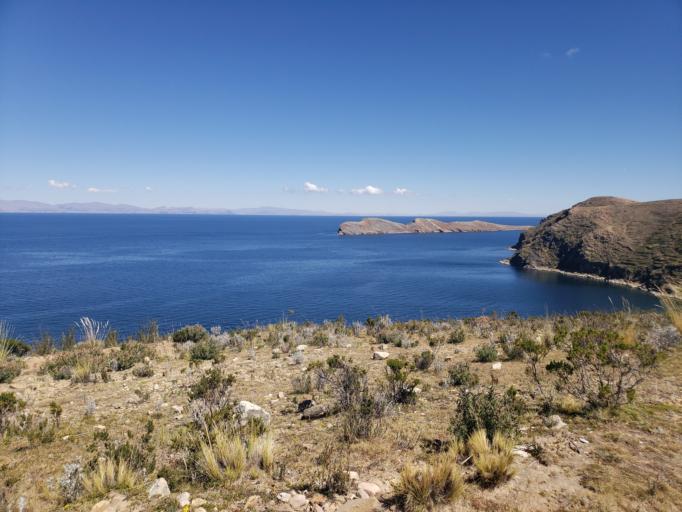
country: BO
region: La Paz
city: Yumani
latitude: -15.9909
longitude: -69.2019
